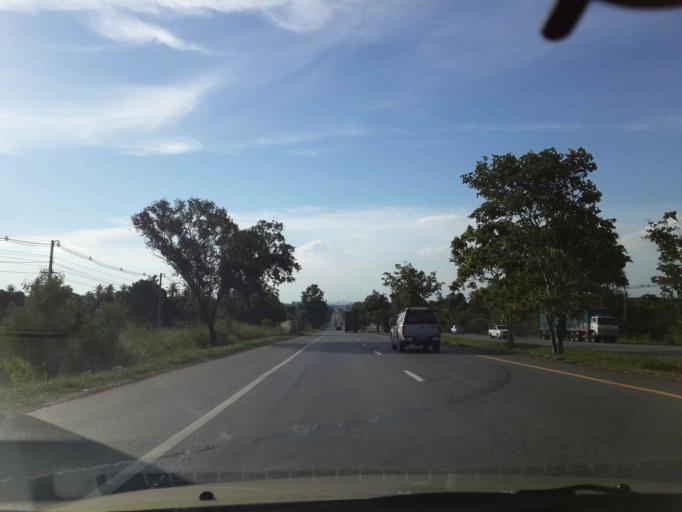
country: TH
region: Chon Buri
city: Phatthaya
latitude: 12.9325
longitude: 101.0000
